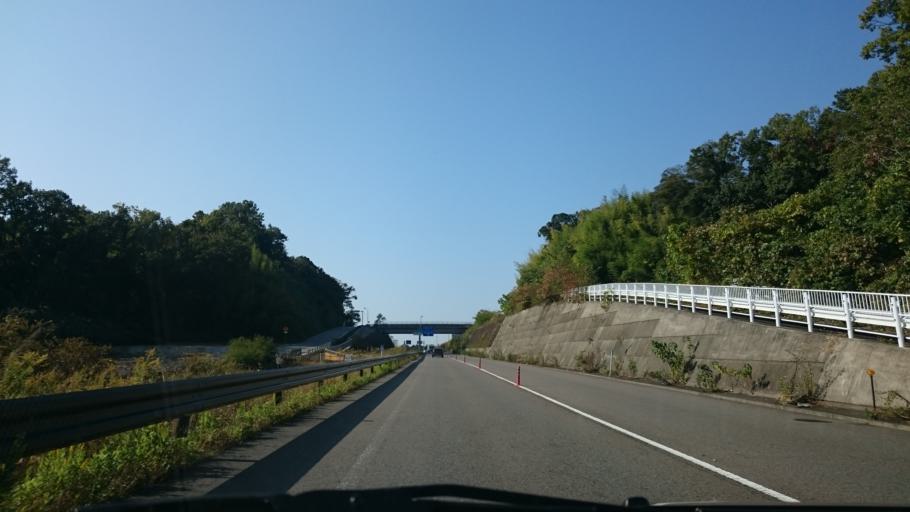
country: JP
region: Gifu
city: Minokamo
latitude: 35.4846
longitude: 137.0522
